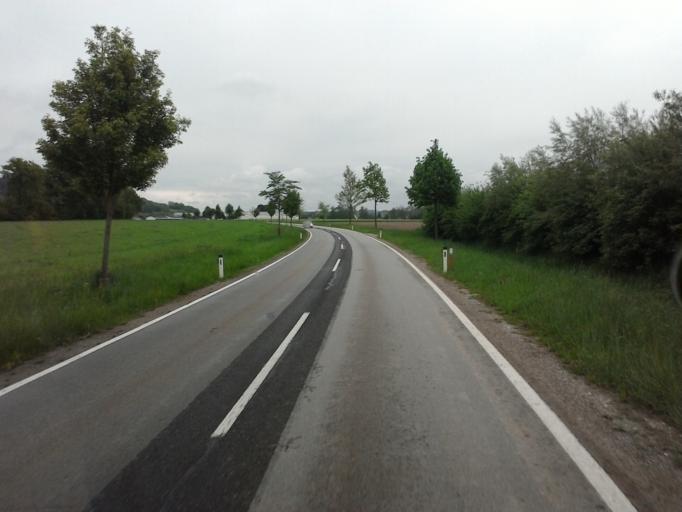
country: AT
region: Upper Austria
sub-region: Politischer Bezirk Scharding
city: Sankt Marienkirchen bei Schaerding
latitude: 48.3263
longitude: 13.4153
